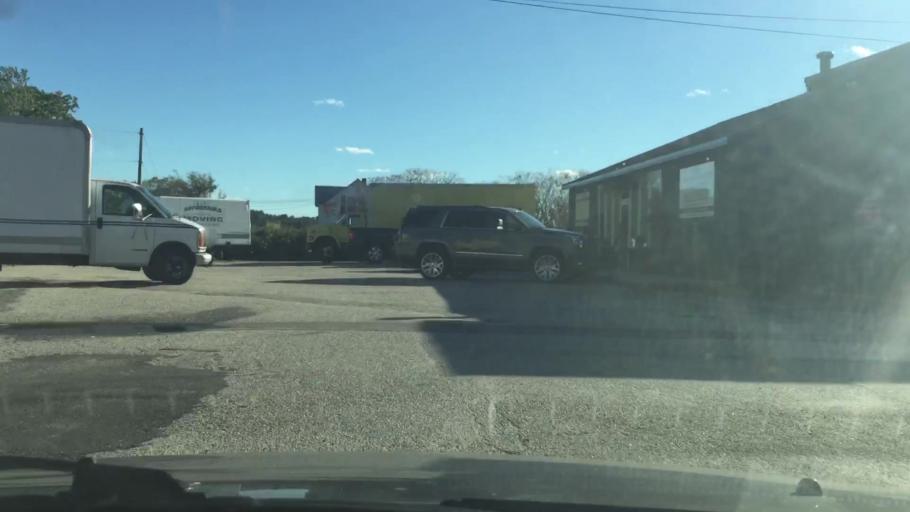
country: US
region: New Hampshire
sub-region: Cheshire County
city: Keene
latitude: 42.9030
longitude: -72.2655
